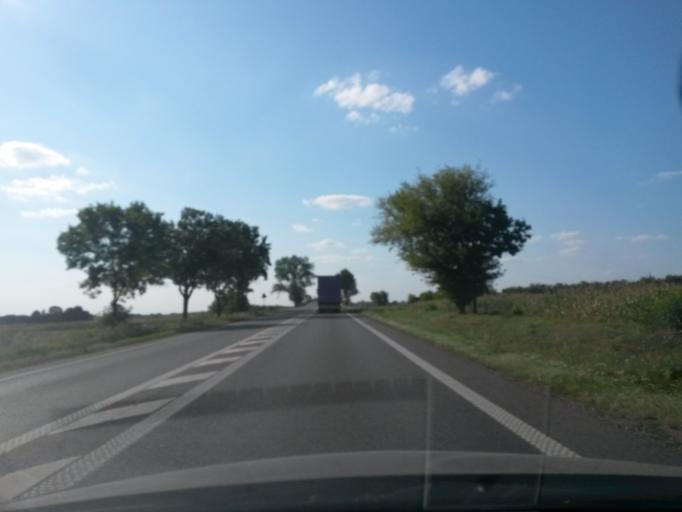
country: PL
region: Masovian Voivodeship
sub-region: Powiat sierpecki
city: Rosciszewo
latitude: 52.8347
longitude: 19.7431
